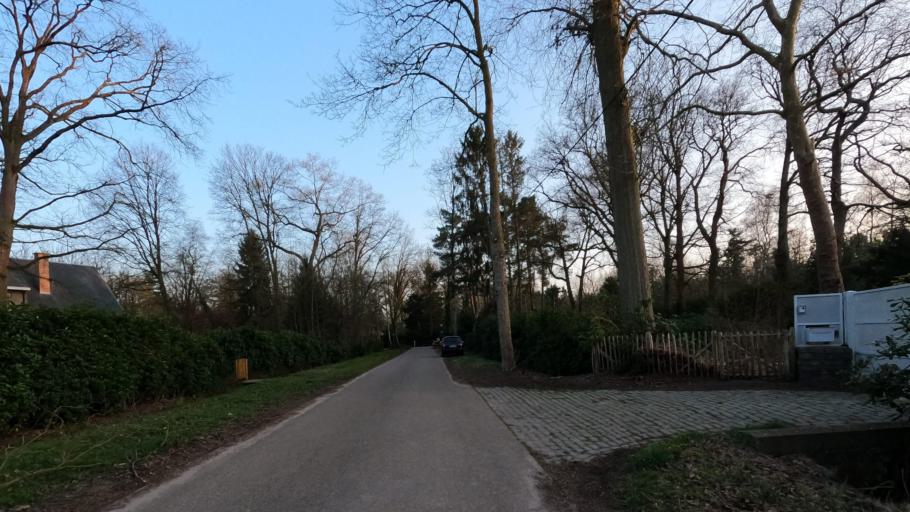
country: BE
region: Flanders
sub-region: Provincie Antwerpen
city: Schilde
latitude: 51.2729
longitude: 4.6111
